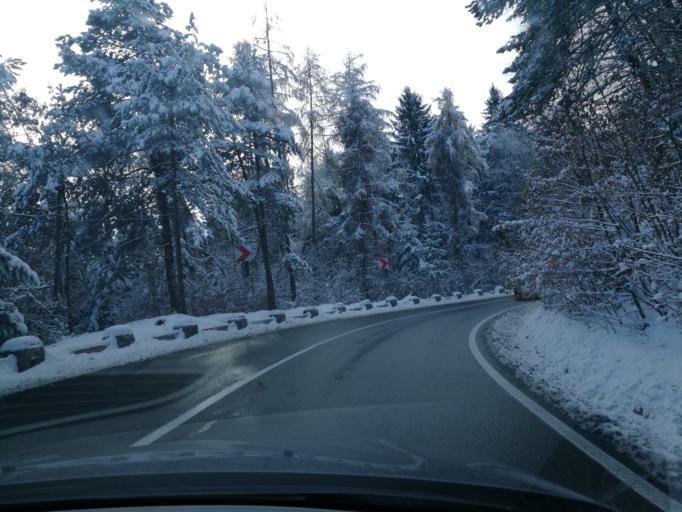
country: RO
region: Brasov
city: Brasov
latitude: 45.6313
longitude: 25.5578
